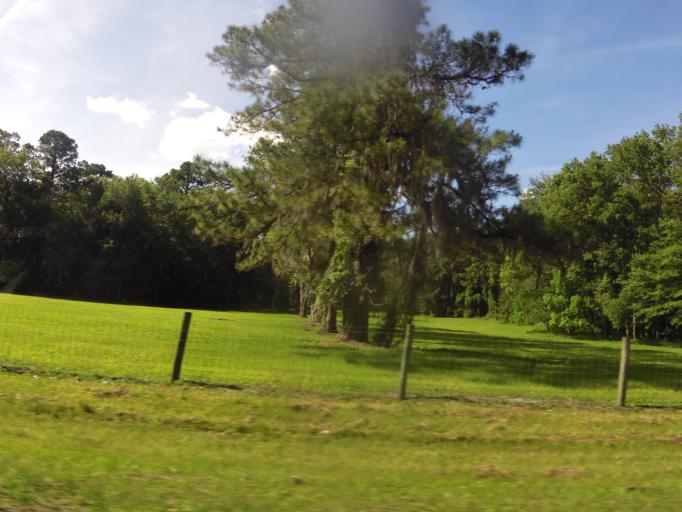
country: US
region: Florida
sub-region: Nassau County
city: Callahan
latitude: 30.5605
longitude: -81.8544
